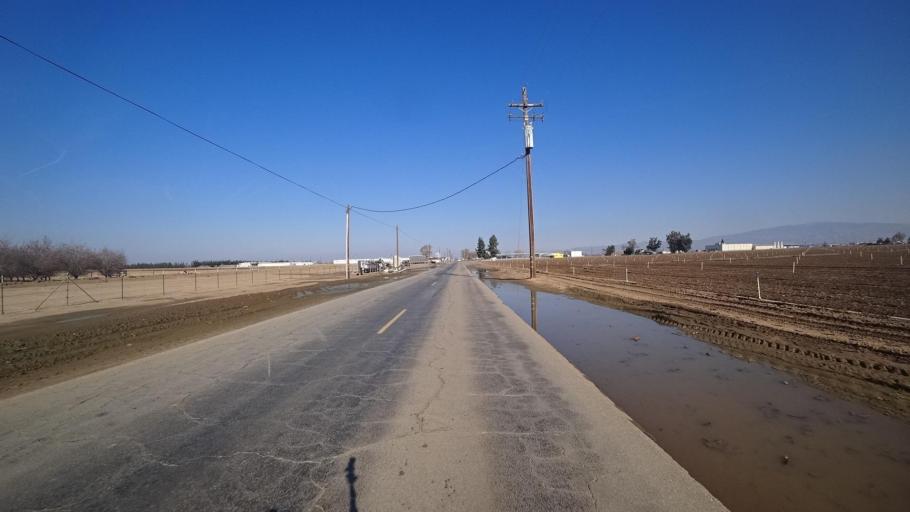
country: US
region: California
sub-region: Kern County
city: Weedpatch
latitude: 35.2481
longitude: -118.8964
